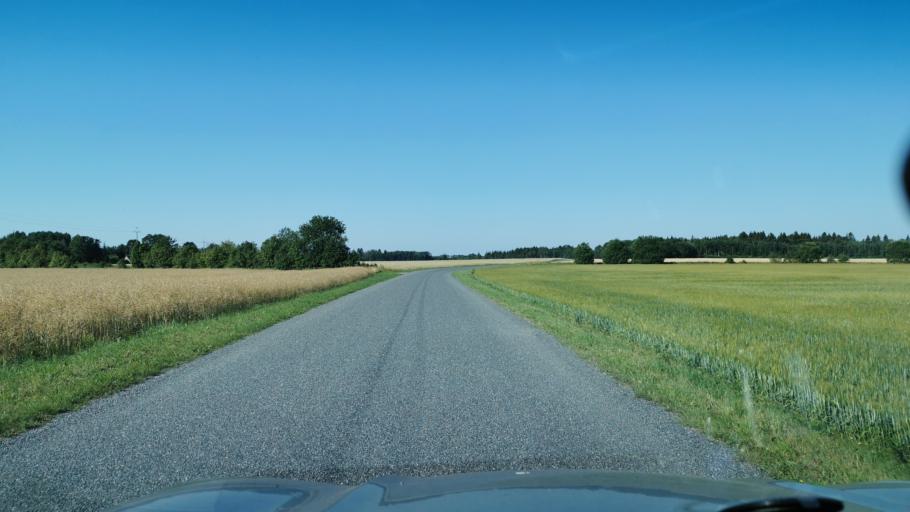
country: EE
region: Harju
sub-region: Paldiski linn
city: Paldiski
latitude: 59.2146
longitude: 24.0392
